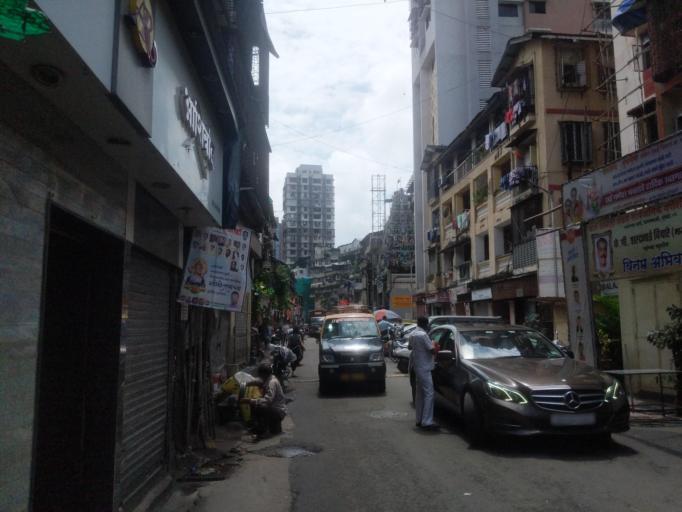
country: IN
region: Maharashtra
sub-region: Mumbai Suburban
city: Mumbai
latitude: 18.9525
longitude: 72.8254
